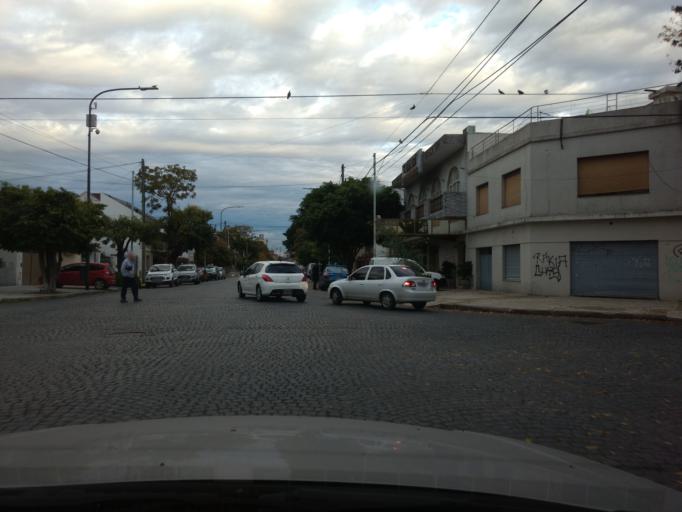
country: AR
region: Buenos Aires F.D.
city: Villa Santa Rita
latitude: -34.6324
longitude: -58.4959
